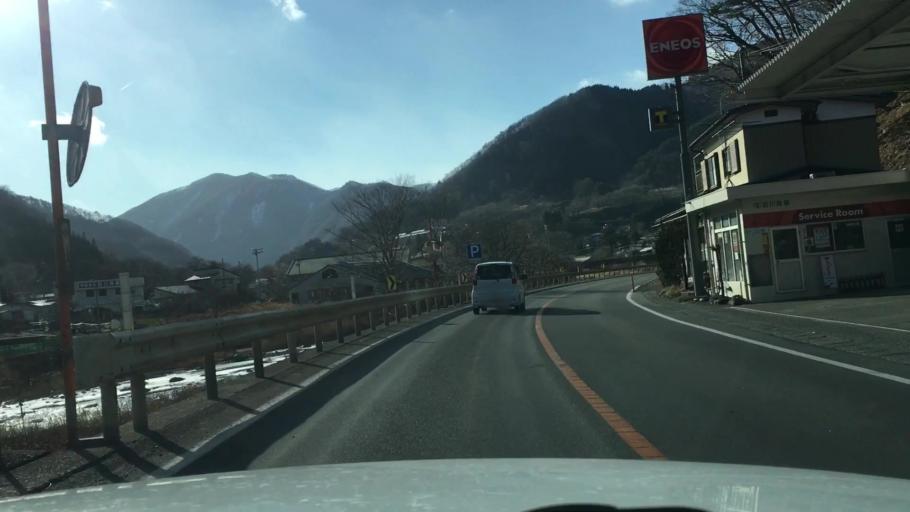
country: JP
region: Iwate
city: Miyako
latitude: 39.5999
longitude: 141.6853
